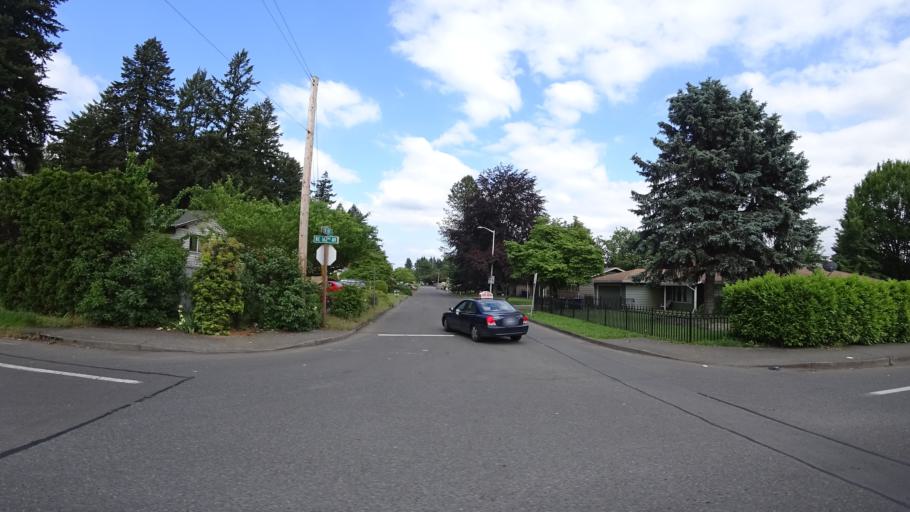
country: US
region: Oregon
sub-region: Multnomah County
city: Fairview
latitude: 45.5274
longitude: -122.4963
